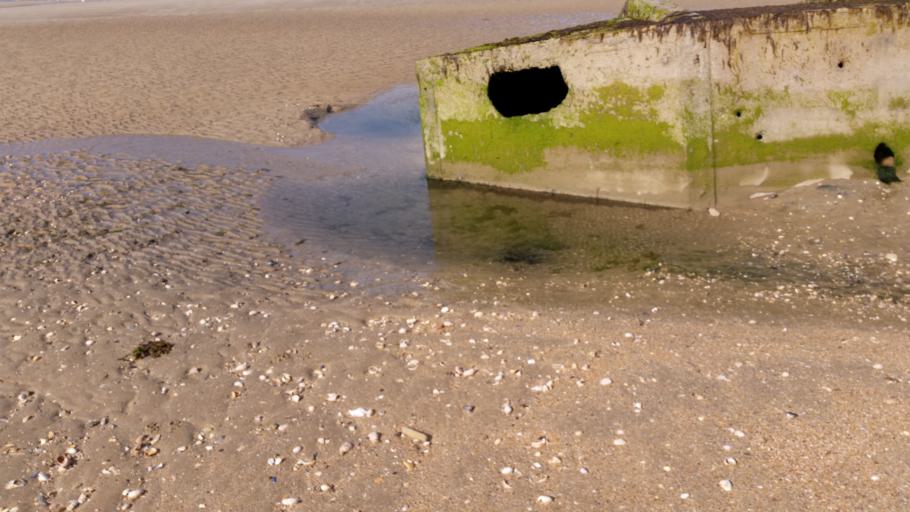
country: FR
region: Lower Normandy
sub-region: Departement de la Manche
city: Sainte-Mere-Eglise
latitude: 49.4476
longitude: -1.2118
